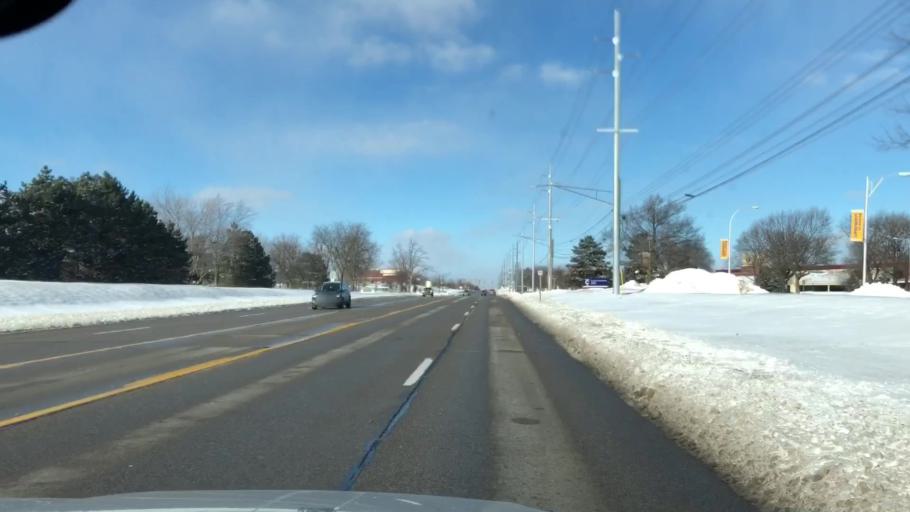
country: US
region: Michigan
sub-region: Wayne County
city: Northville
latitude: 42.4186
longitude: -83.4327
